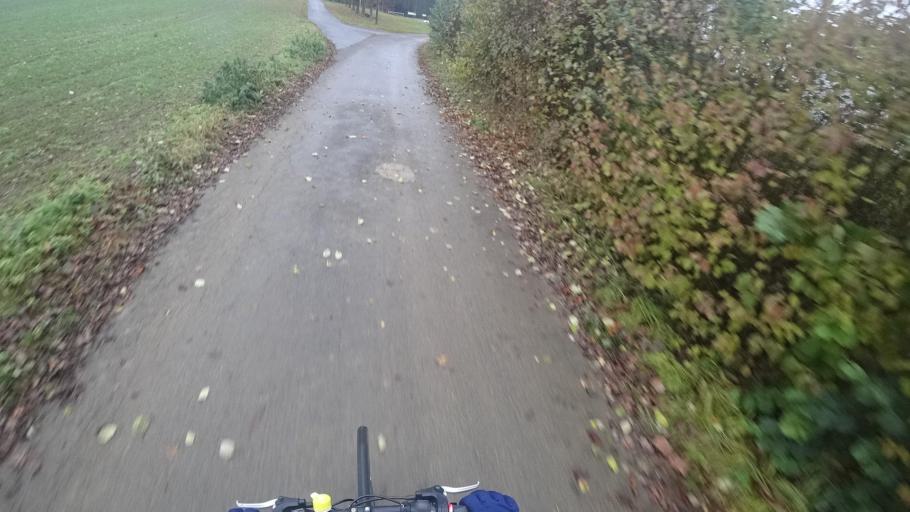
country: DE
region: Rheinland-Pfalz
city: Ney
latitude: 50.1791
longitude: 7.5336
